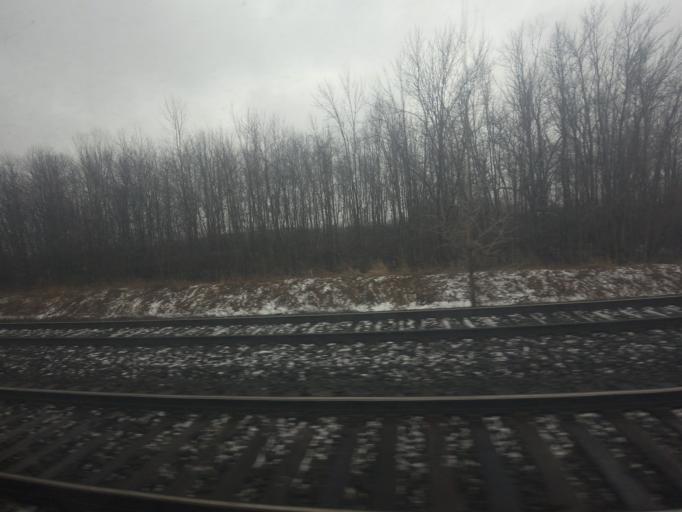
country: CA
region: Ontario
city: Belleville
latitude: 44.1938
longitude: -77.3178
